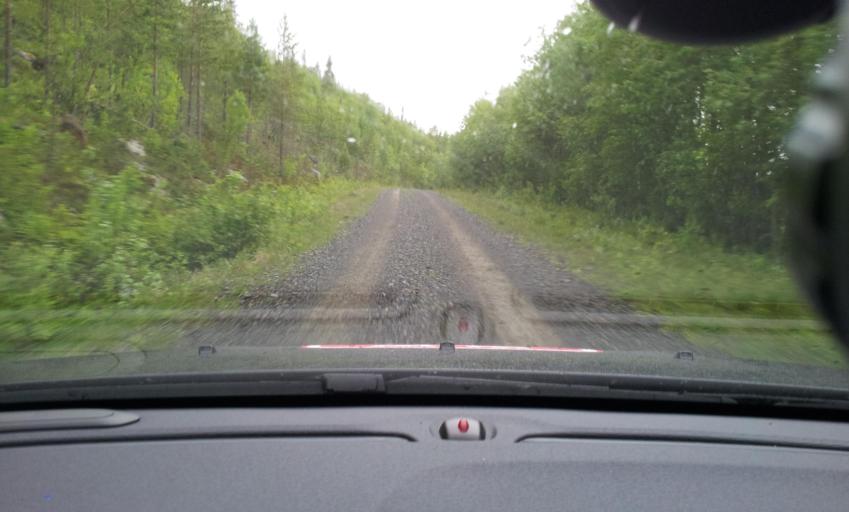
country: SE
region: Jaemtland
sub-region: Are Kommun
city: Jarpen
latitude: 63.1920
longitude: 13.4261
